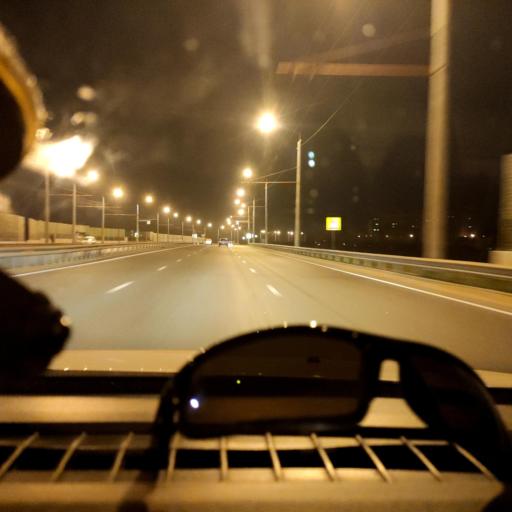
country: RU
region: Samara
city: Samara
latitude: 53.1617
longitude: 50.0884
